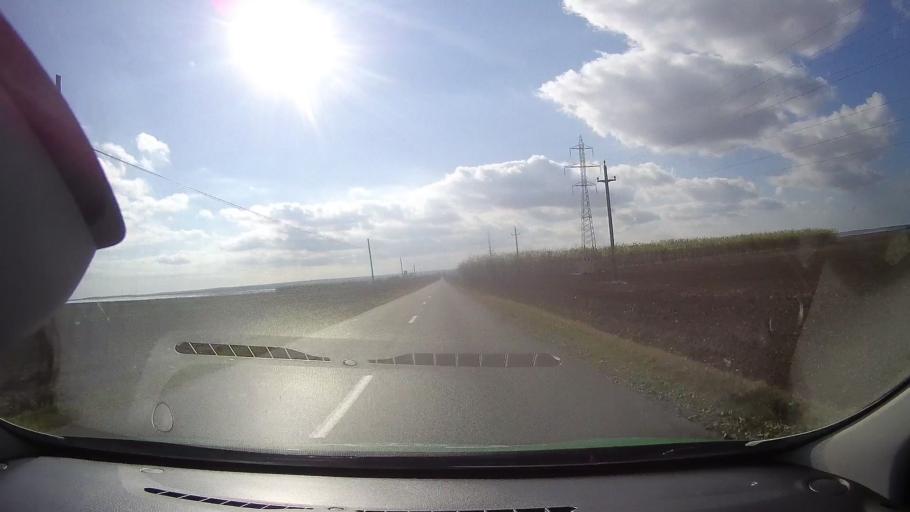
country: RO
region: Constanta
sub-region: Comuna Istria
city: Istria
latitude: 44.5530
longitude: 28.6966
